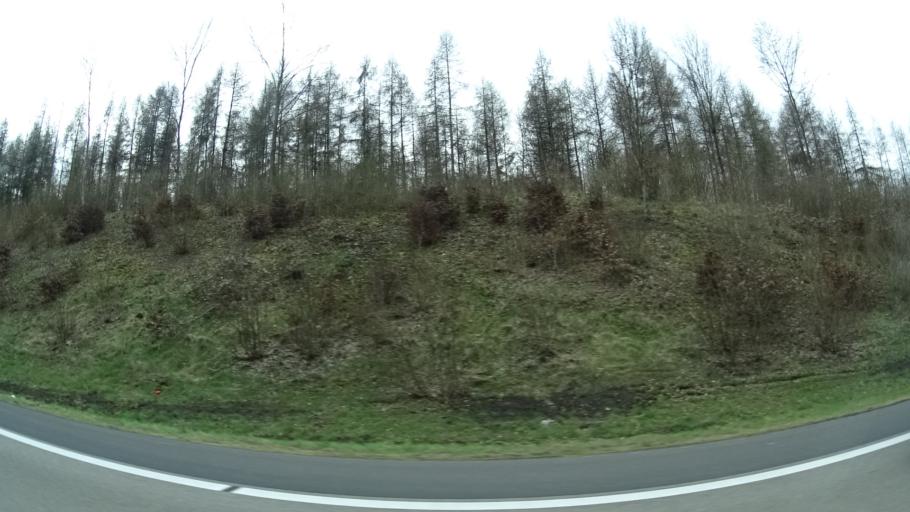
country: DE
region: Hesse
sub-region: Regierungsbezirk Darmstadt
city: Echzell
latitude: 50.3910
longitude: 8.9347
